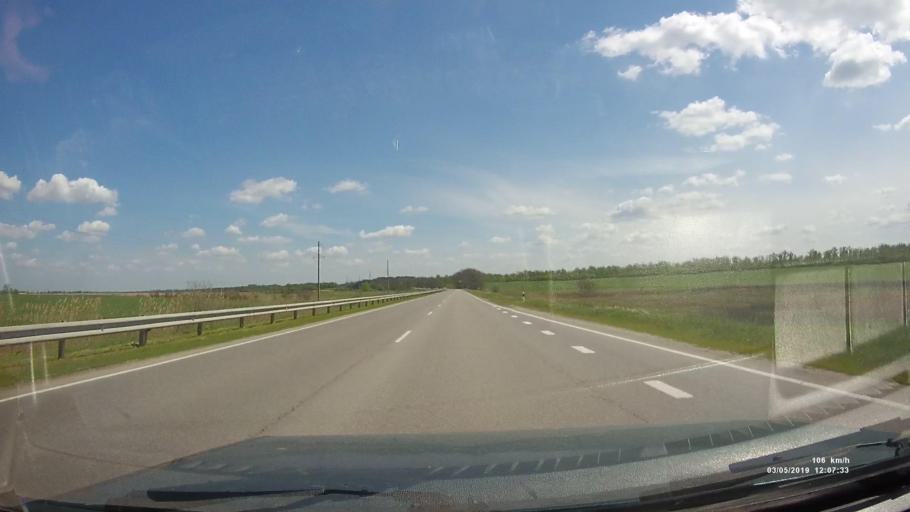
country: RU
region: Rostov
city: Bagayevskaya
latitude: 47.2845
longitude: 40.4775
